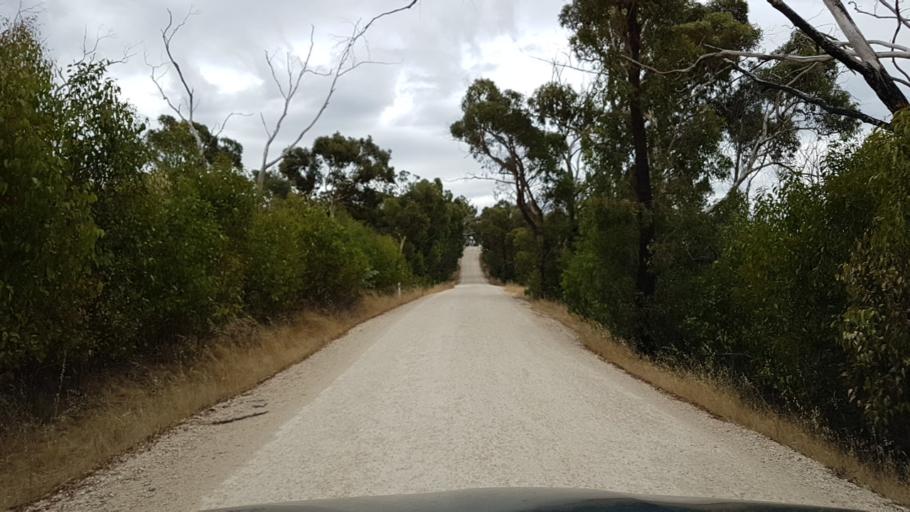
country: AU
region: South Australia
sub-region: Tea Tree Gully
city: Golden Grove
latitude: -34.7831
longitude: 138.8137
